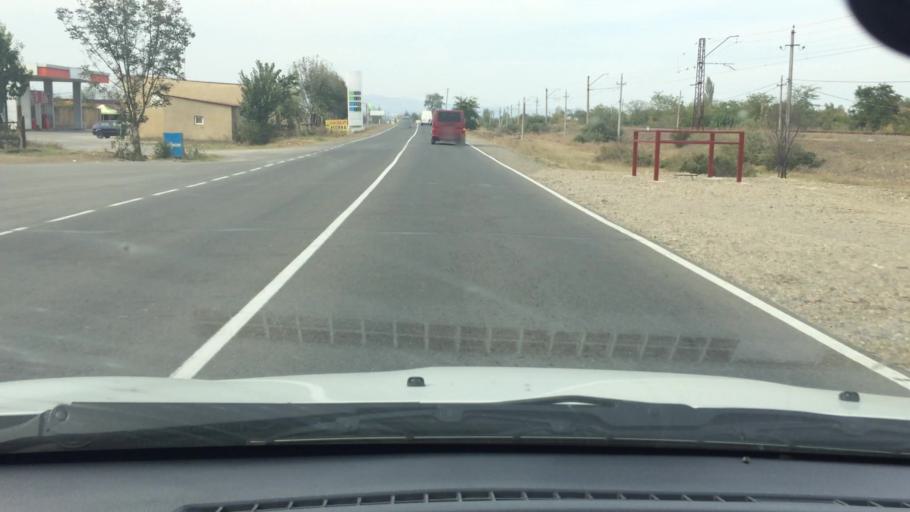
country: GE
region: Kvemo Kartli
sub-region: Marneuli
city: Marneuli
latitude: 41.4369
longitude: 44.8187
